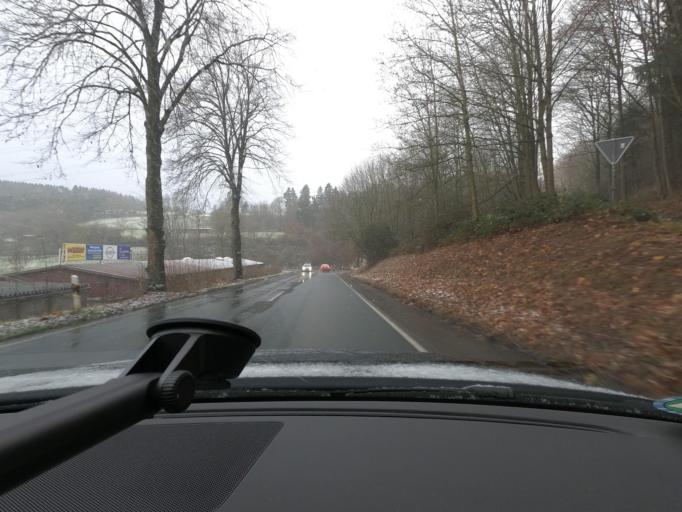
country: DE
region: North Rhine-Westphalia
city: Marsberg
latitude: 51.5033
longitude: 8.8687
